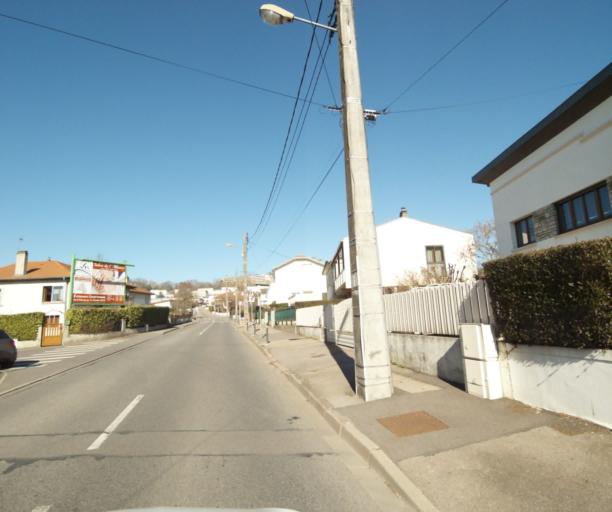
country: FR
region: Lorraine
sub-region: Departement de Meurthe-et-Moselle
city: Saint-Max
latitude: 48.7042
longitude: 6.1991
